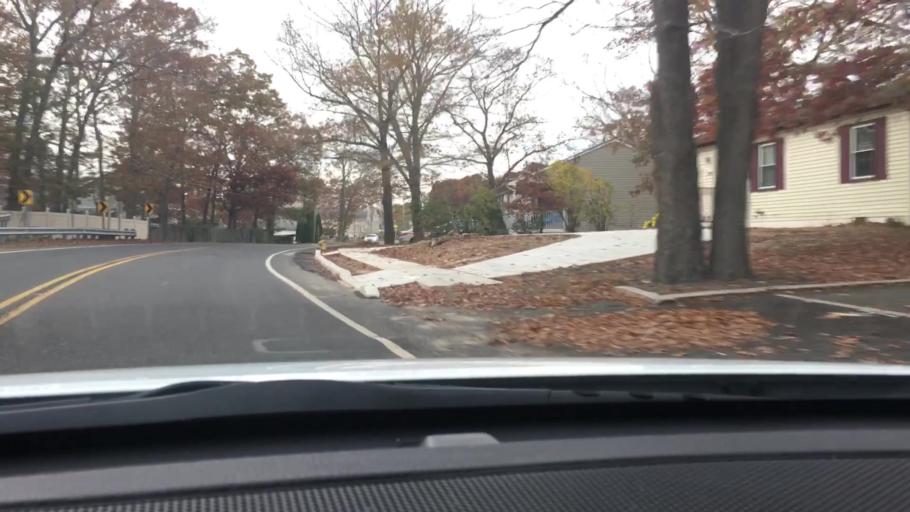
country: US
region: New Jersey
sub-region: Atlantic County
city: Northfield
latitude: 39.3852
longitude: -74.5453
